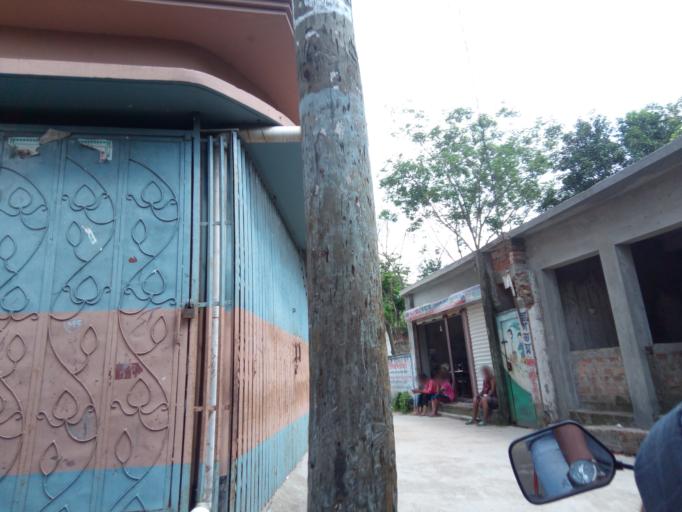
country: BD
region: Dhaka
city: Azimpur
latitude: 23.7373
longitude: 90.3368
